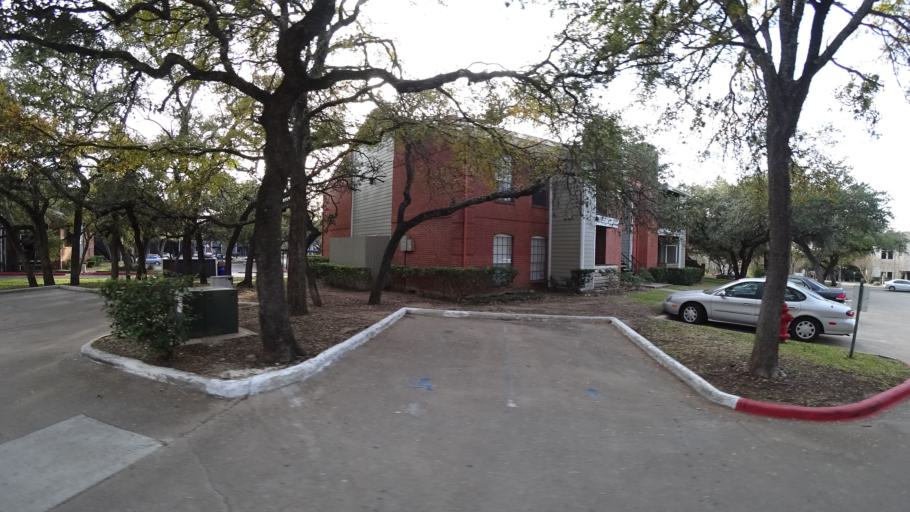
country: US
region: Texas
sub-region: Williamson County
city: Jollyville
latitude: 30.3939
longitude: -97.7549
